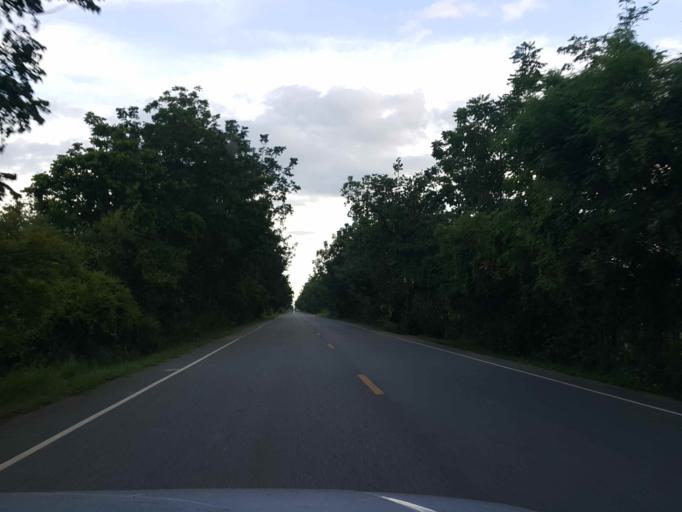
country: TH
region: Sukhothai
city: Sawankhalok
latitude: 17.3169
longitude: 99.7352
